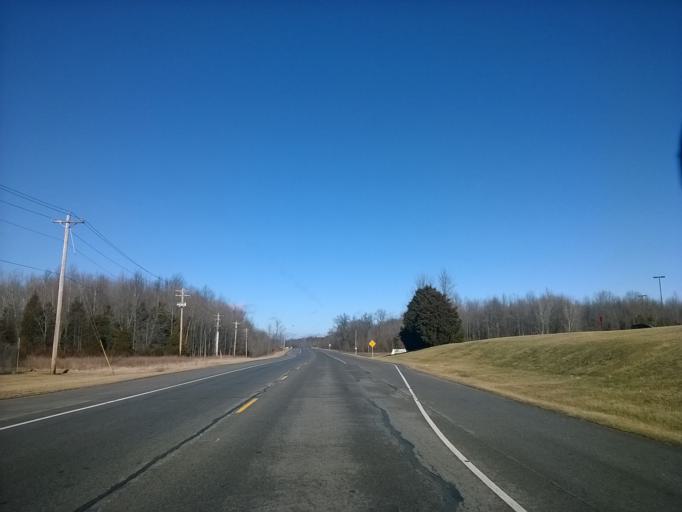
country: US
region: Indiana
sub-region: Scott County
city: Austin
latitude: 38.7593
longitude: -85.8149
